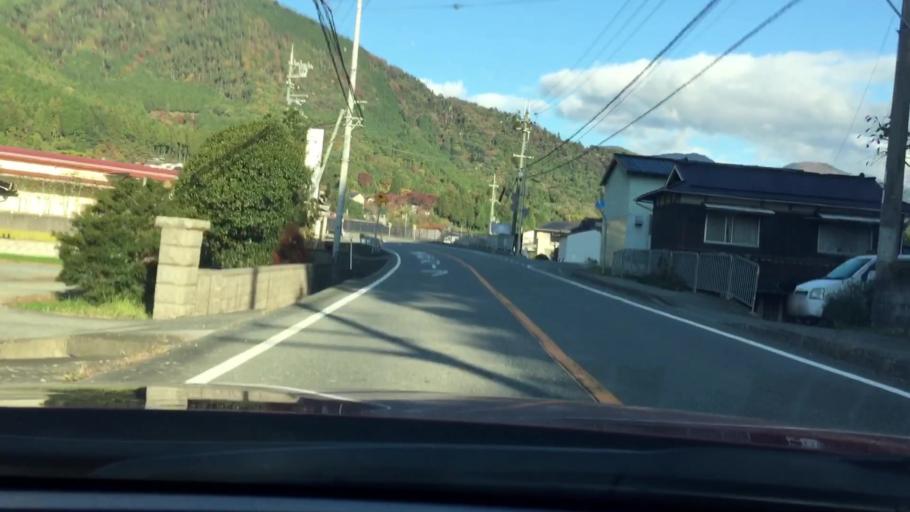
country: JP
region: Hyogo
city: Yamazakicho-nakabirose
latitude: 35.1161
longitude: 134.5706
